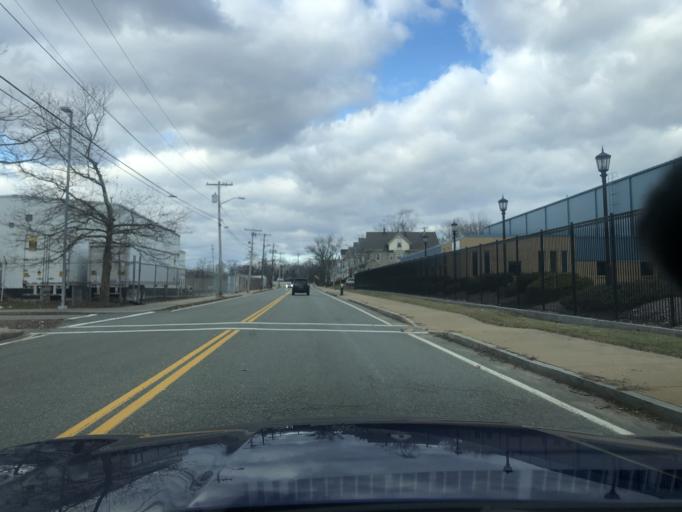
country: US
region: Massachusetts
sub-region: Plymouth County
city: Brockton
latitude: 42.1071
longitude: -71.0210
